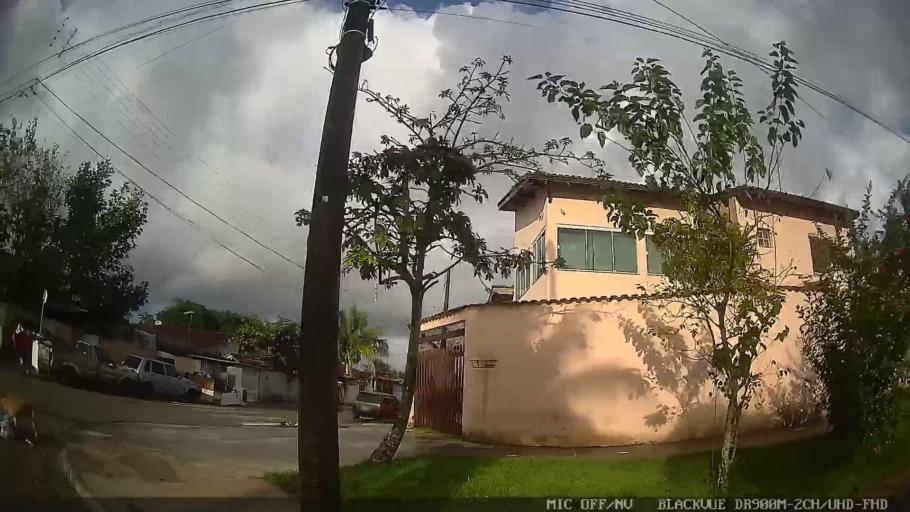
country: BR
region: Sao Paulo
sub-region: Itanhaem
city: Itanhaem
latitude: -24.2033
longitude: -46.8728
